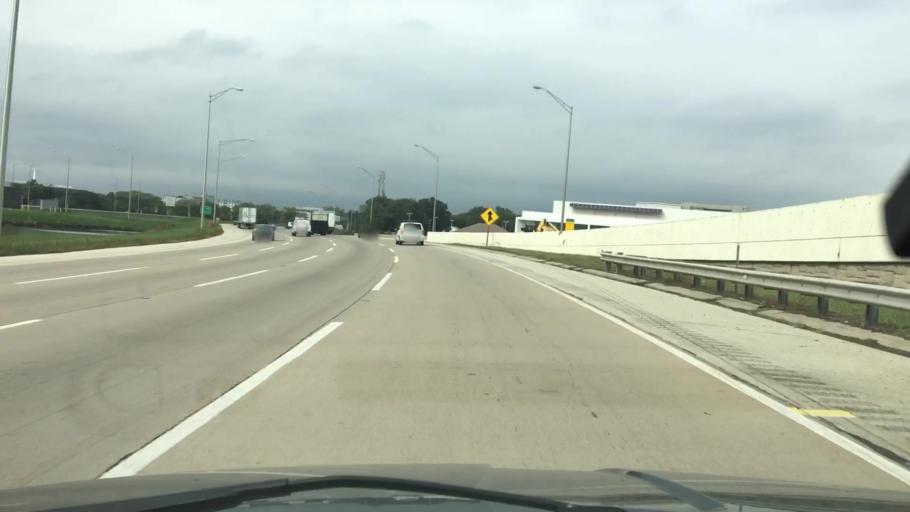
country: US
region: Illinois
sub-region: Lake County
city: Riverwoods
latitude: 42.1547
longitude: -87.8721
